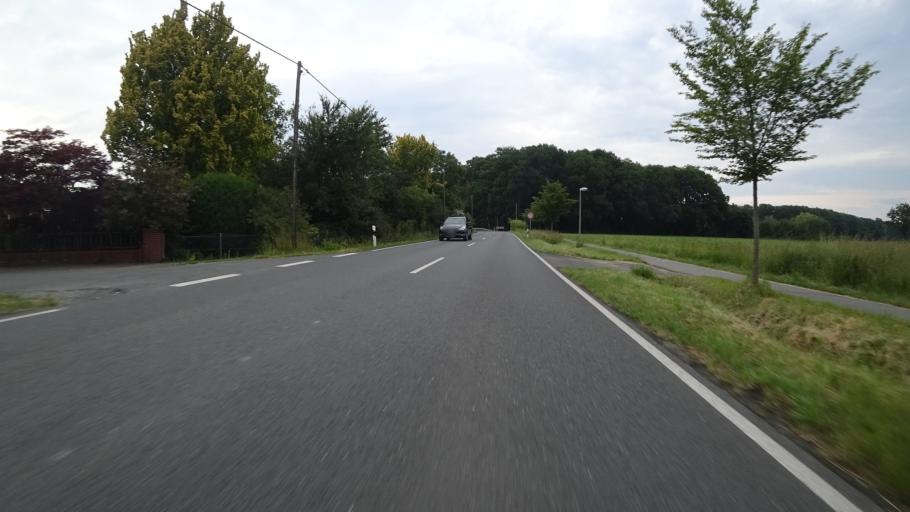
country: DE
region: North Rhine-Westphalia
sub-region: Regierungsbezirk Detmold
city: Guetersloh
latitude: 51.9408
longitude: 8.3801
